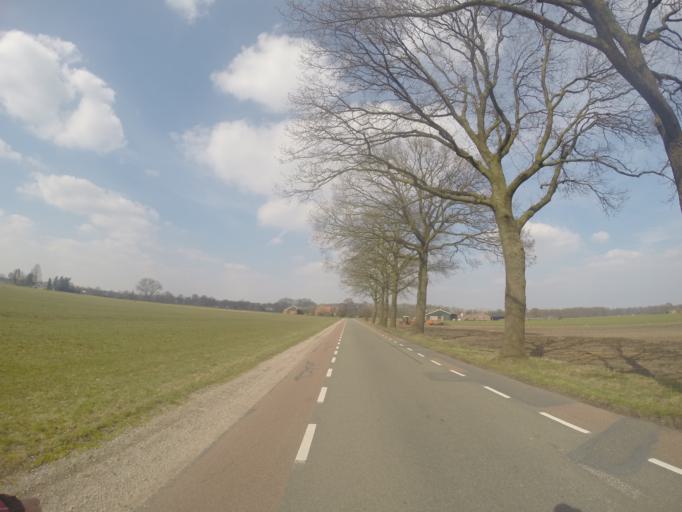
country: NL
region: Gelderland
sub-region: Gemeente Lochem
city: Almen
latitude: 52.1526
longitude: 6.3143
